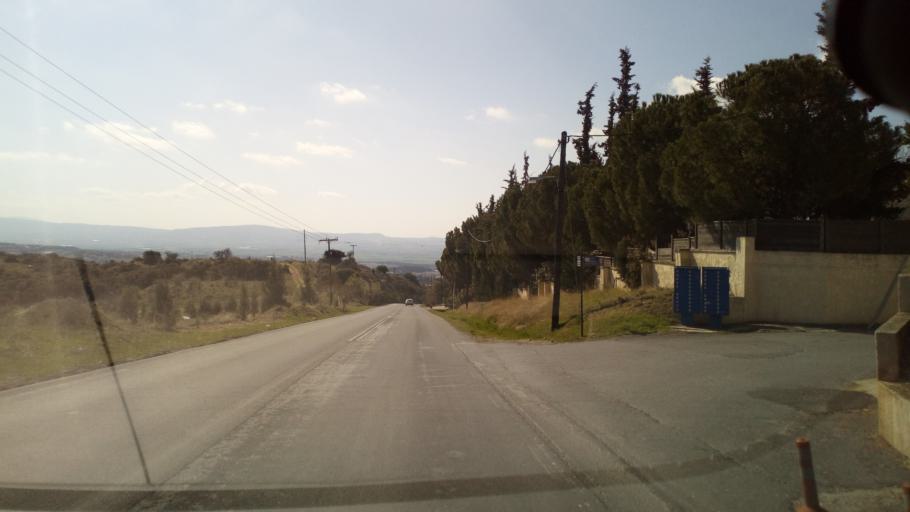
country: GR
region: Central Macedonia
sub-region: Nomos Thessalonikis
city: Panorama
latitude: 40.5727
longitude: 23.0248
